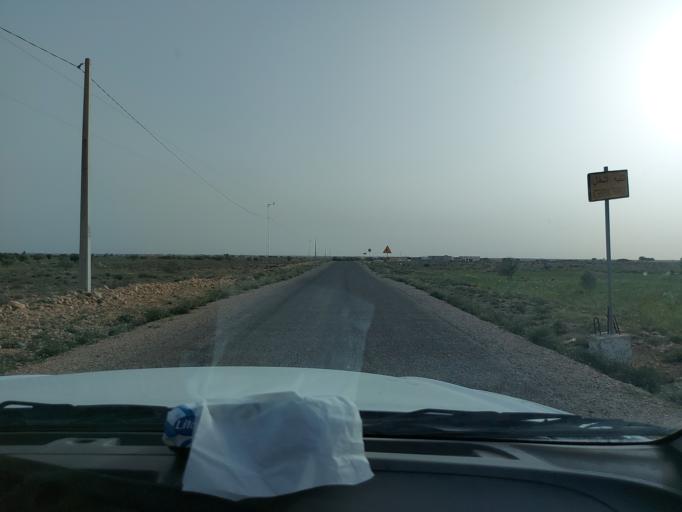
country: TN
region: Madanin
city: Medenine
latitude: 33.3448
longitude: 10.5890
